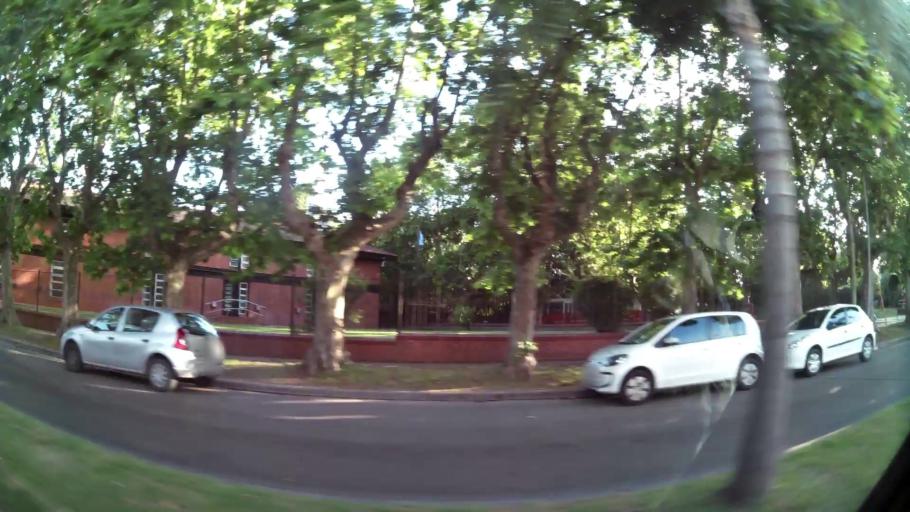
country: AR
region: Buenos Aires
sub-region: Partido de Tigre
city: Tigre
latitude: -34.4551
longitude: -58.6328
